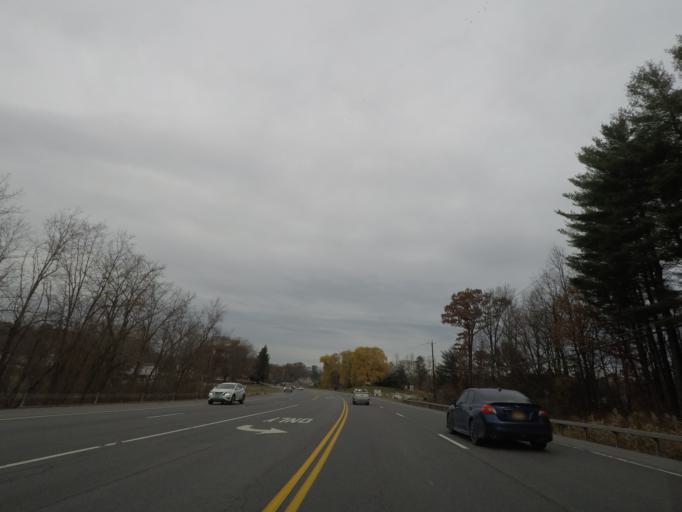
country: US
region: New York
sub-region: Saratoga County
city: Country Knolls
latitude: 42.8995
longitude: -73.7720
